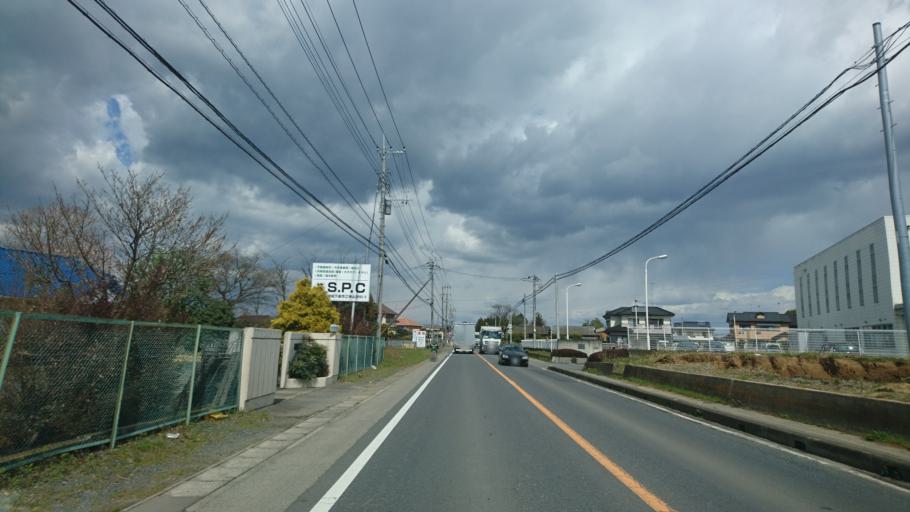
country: JP
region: Ibaraki
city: Yuki
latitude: 36.2245
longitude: 139.9331
